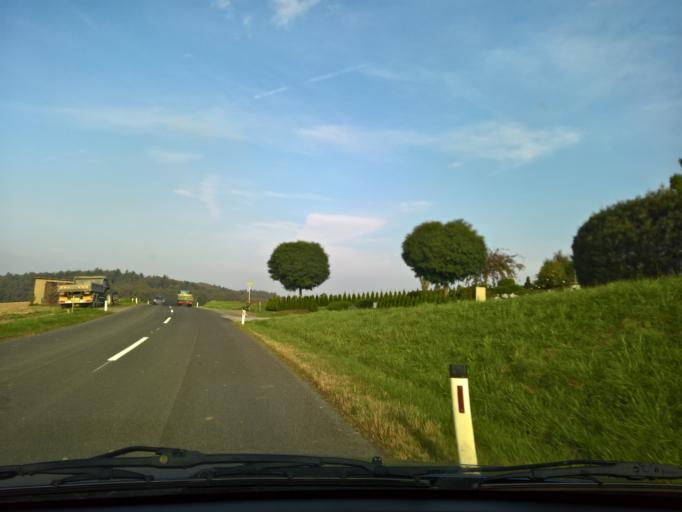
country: AT
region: Styria
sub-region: Politischer Bezirk Leibnitz
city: Pistorf
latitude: 46.7659
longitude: 15.3530
